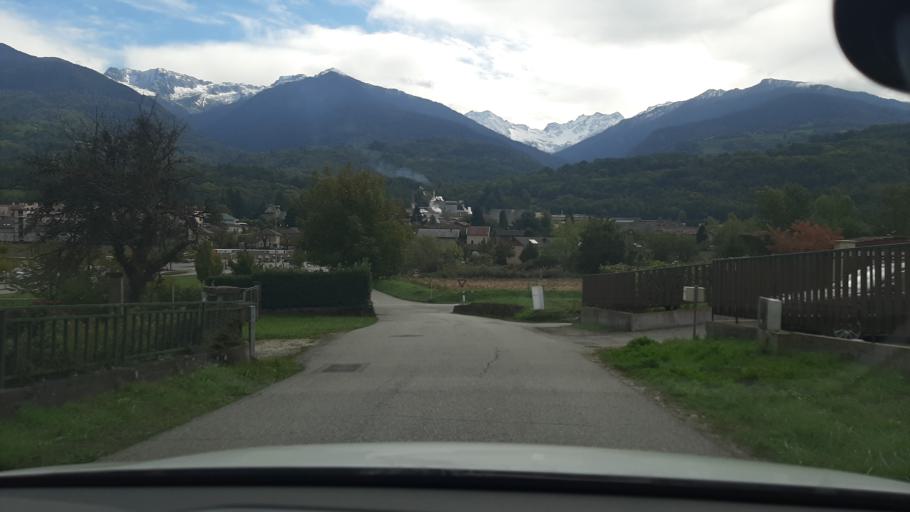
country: FR
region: Rhone-Alpes
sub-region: Departement de la Savoie
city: La Rochette
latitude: 45.4587
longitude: 6.1092
